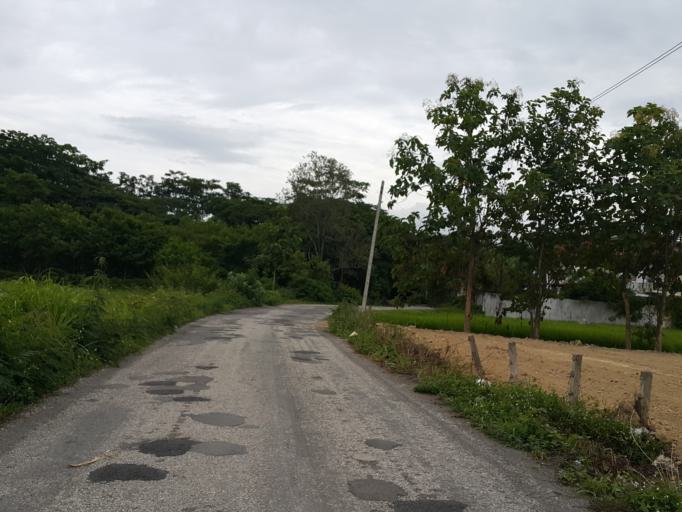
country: TH
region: Chiang Mai
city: San Sai
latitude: 18.8562
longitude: 99.1192
